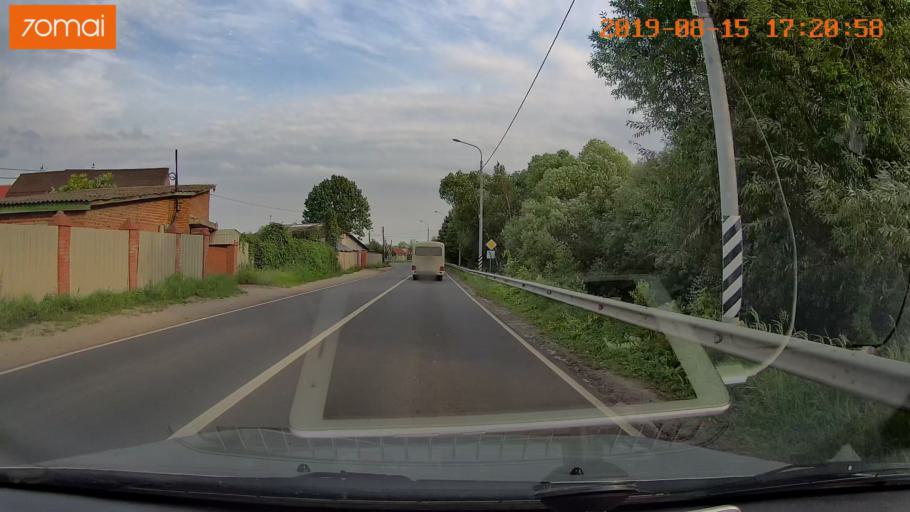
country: RU
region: Moskovskaya
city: Ashitkovo
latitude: 55.4222
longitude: 38.5628
